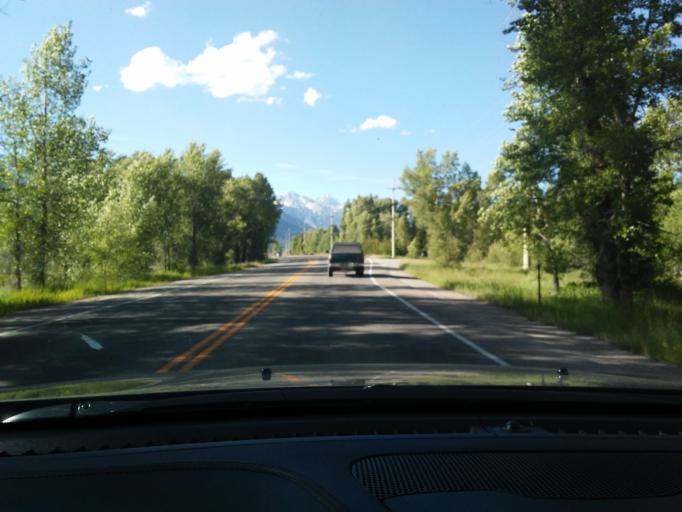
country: US
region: Wyoming
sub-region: Teton County
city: Moose Wilson Road
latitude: 43.5445
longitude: -110.8220
